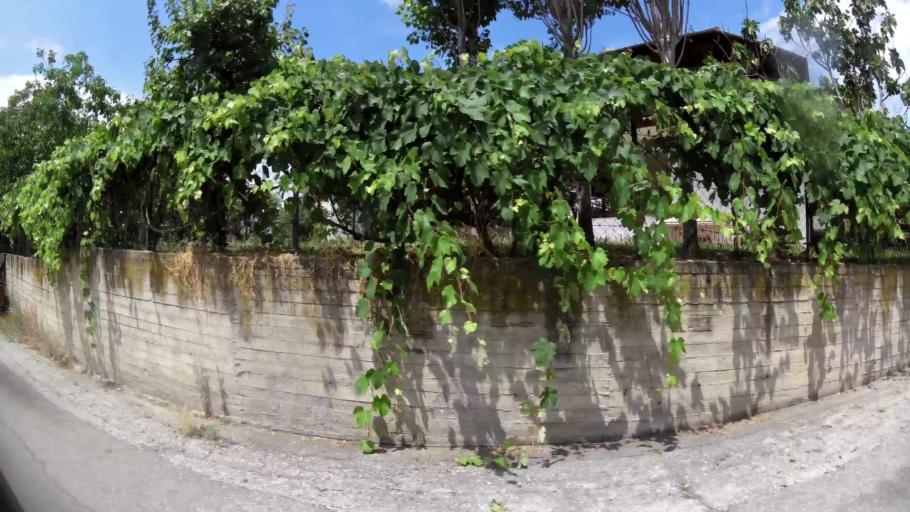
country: GR
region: Central Macedonia
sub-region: Nomos Pierias
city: Katerini
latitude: 40.2624
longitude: 22.5001
